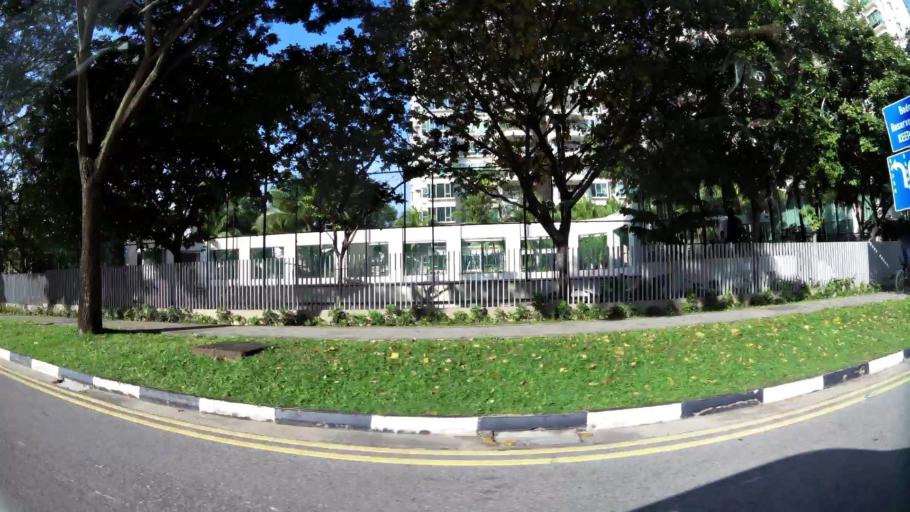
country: SG
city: Singapore
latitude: 1.3372
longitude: 103.9330
